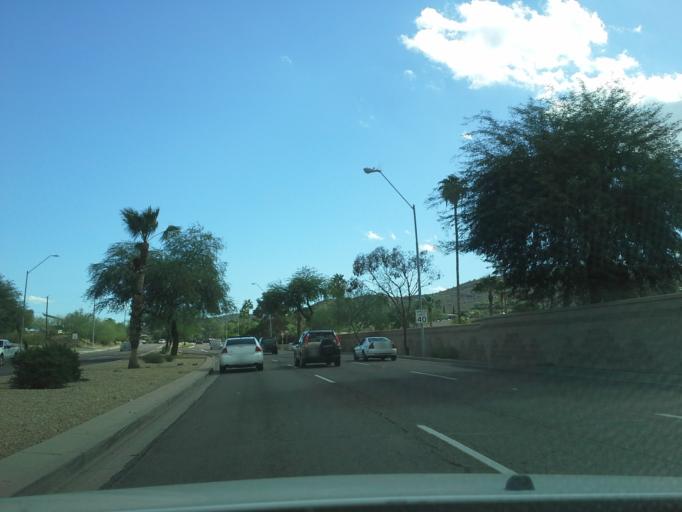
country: US
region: Arizona
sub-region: Maricopa County
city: Glendale
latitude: 33.6085
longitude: -112.0908
